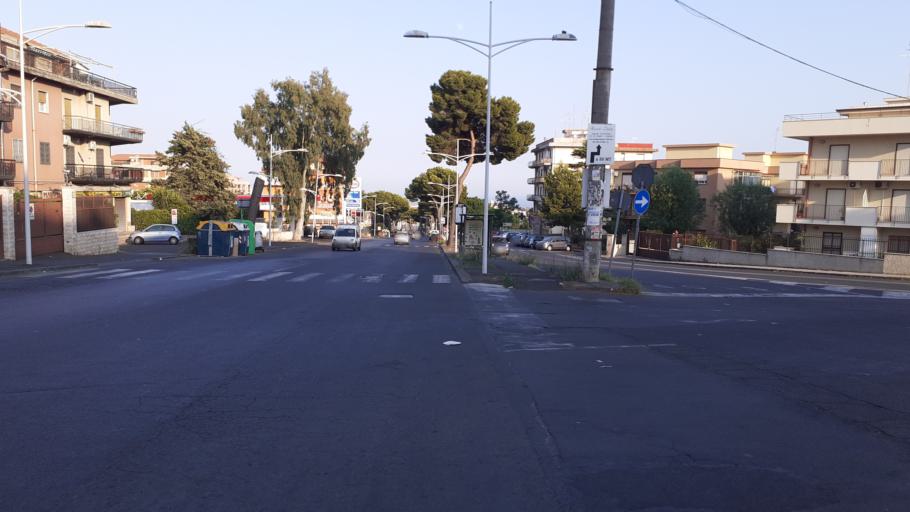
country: IT
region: Sicily
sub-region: Catania
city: Misterbianco
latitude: 37.5069
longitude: 15.0514
